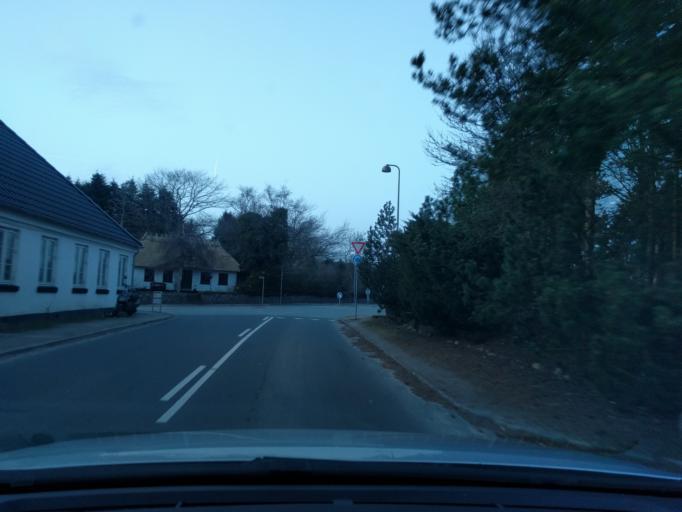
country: DK
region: South Denmark
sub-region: Odense Kommune
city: Bellinge
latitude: 55.3475
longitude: 10.2694
